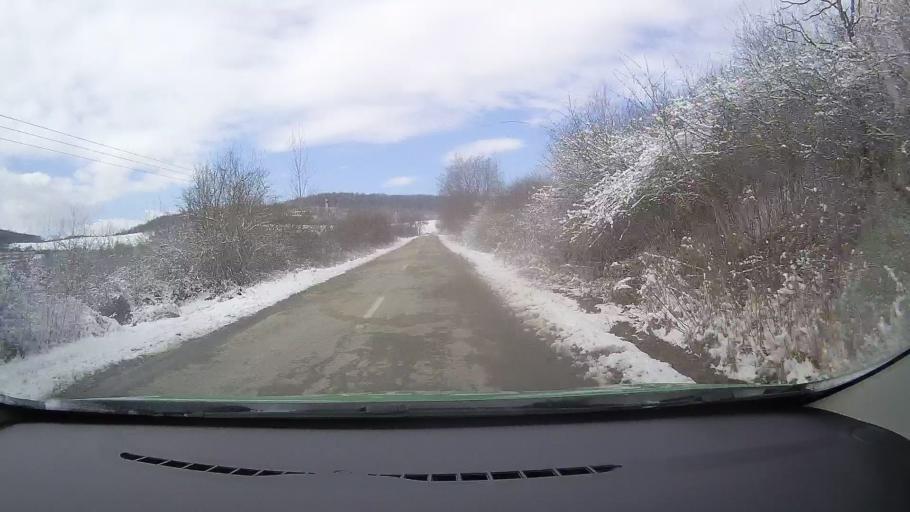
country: RO
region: Sibiu
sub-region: Comuna Altina
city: Altina
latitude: 45.9937
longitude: 24.4430
